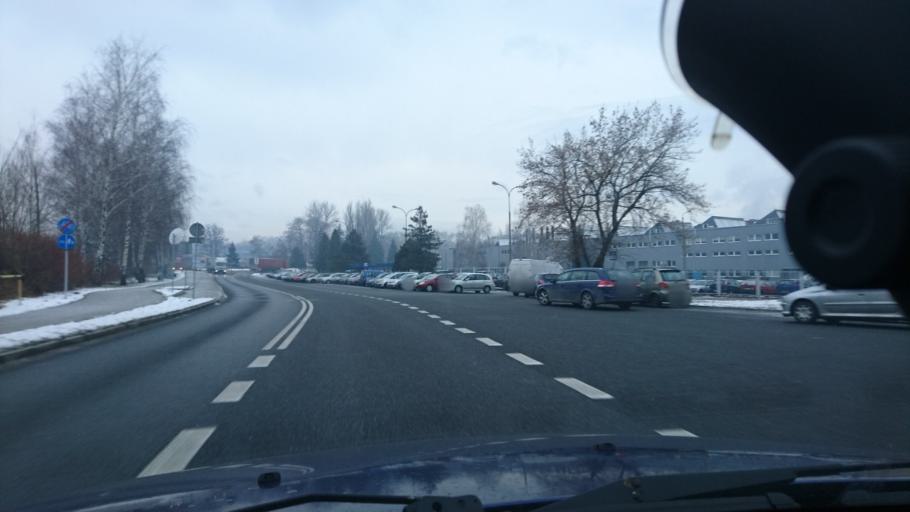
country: PL
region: Silesian Voivodeship
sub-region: Bielsko-Biala
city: Bielsko-Biala
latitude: 49.8425
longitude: 19.0467
